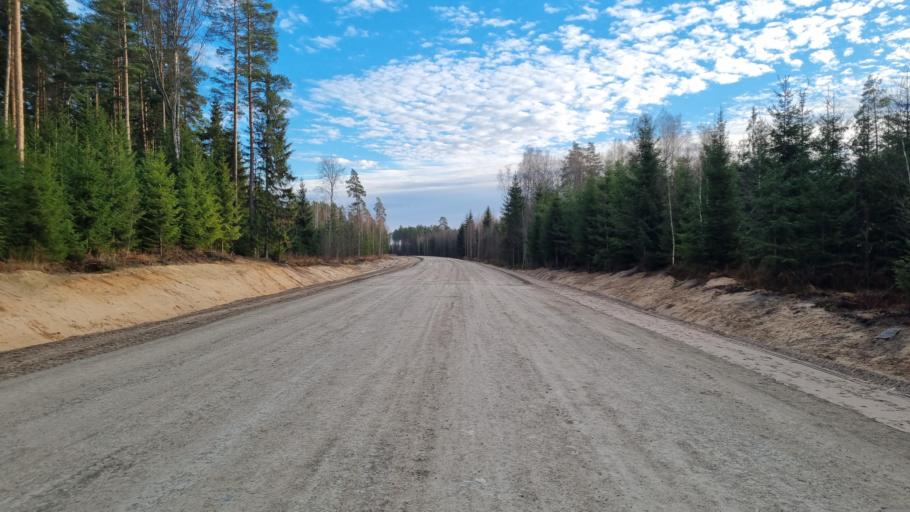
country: LV
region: Kekava
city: Kekava
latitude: 56.7925
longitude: 24.2134
